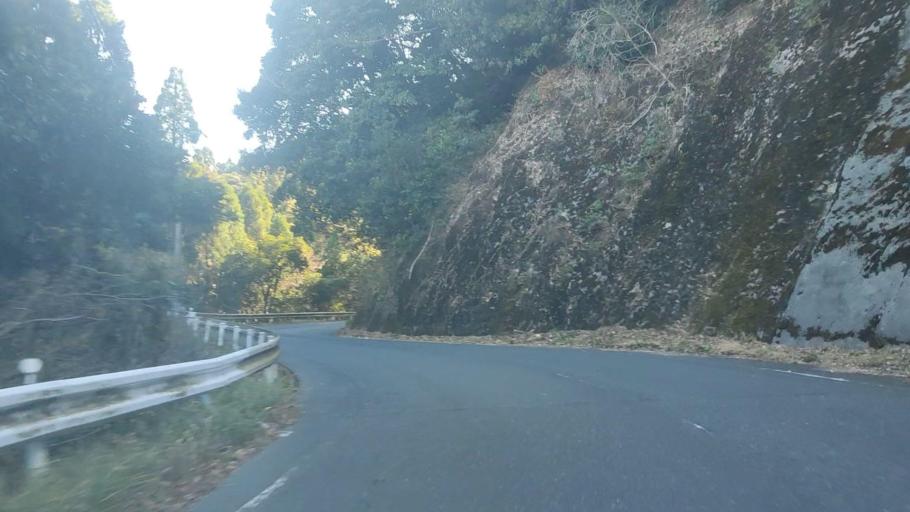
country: JP
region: Kagoshima
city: Kokubu-matsuki
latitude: 31.6707
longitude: 130.8332
